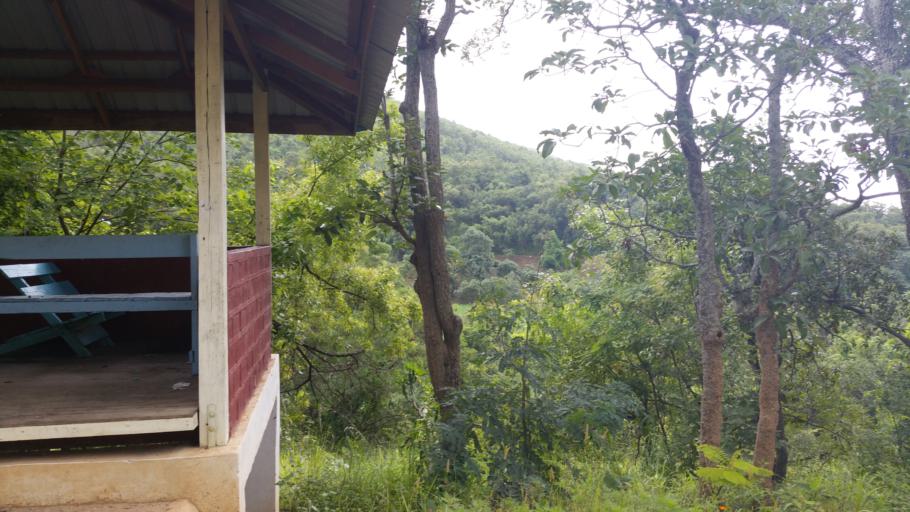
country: MM
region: Shan
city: Taunggyi
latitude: 20.5780
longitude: 96.9573
